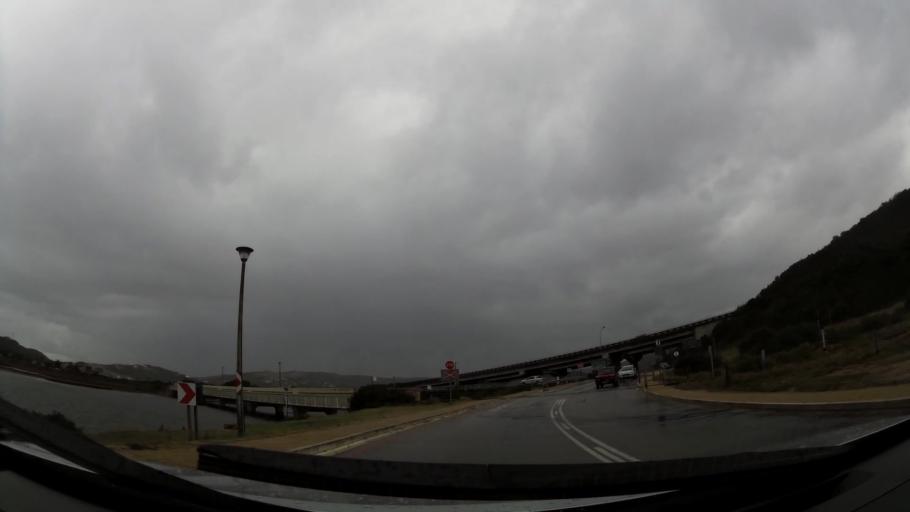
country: ZA
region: Western Cape
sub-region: Eden District Municipality
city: Mossel Bay
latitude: -34.0514
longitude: 22.2323
